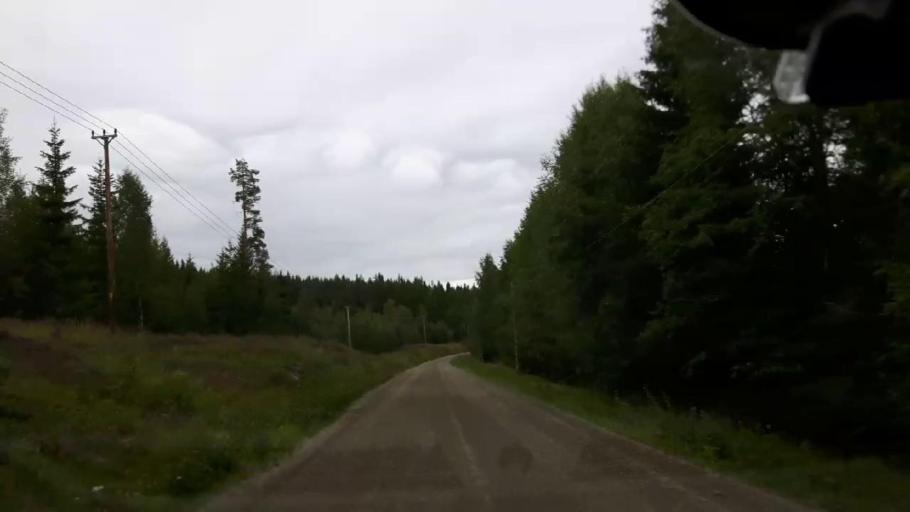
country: SE
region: Jaemtland
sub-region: Braecke Kommun
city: Braecke
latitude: 63.0200
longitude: 15.3746
